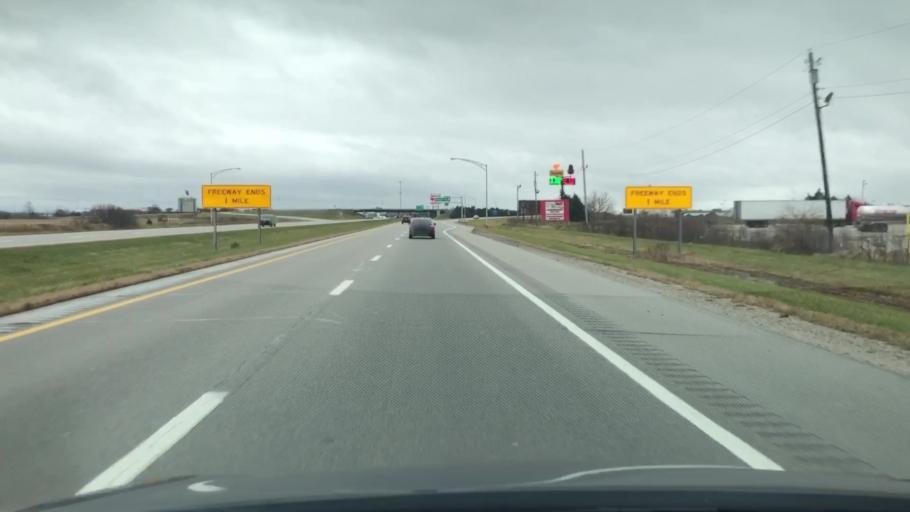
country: US
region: Ohio
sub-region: Wood County
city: Millbury
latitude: 41.5421
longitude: -83.4625
